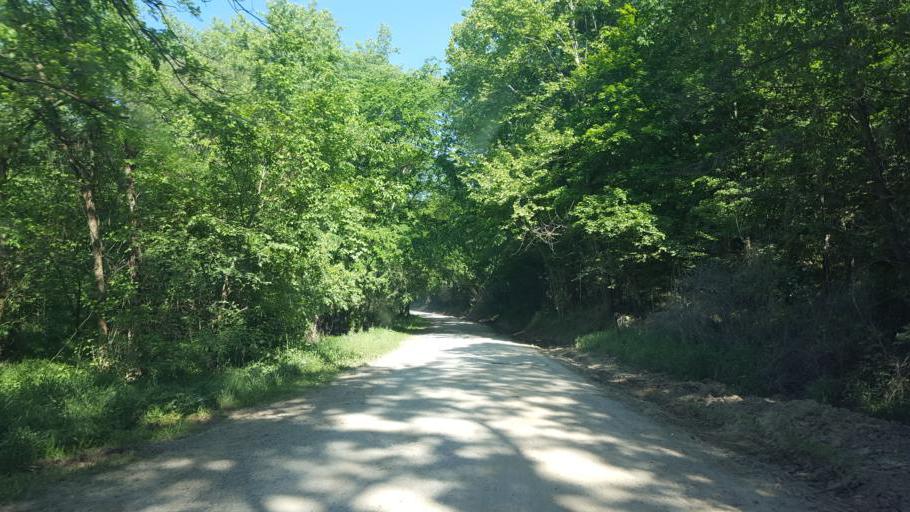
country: US
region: Ohio
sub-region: Jackson County
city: Wellston
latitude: 38.9949
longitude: -82.4138
